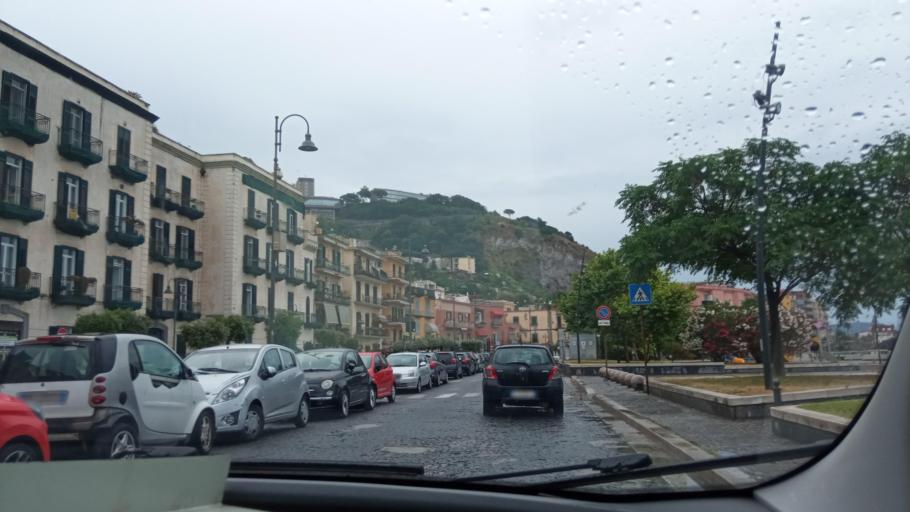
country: IT
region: Campania
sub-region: Provincia di Napoli
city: Pozzuoli
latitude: 40.8211
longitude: 14.1314
